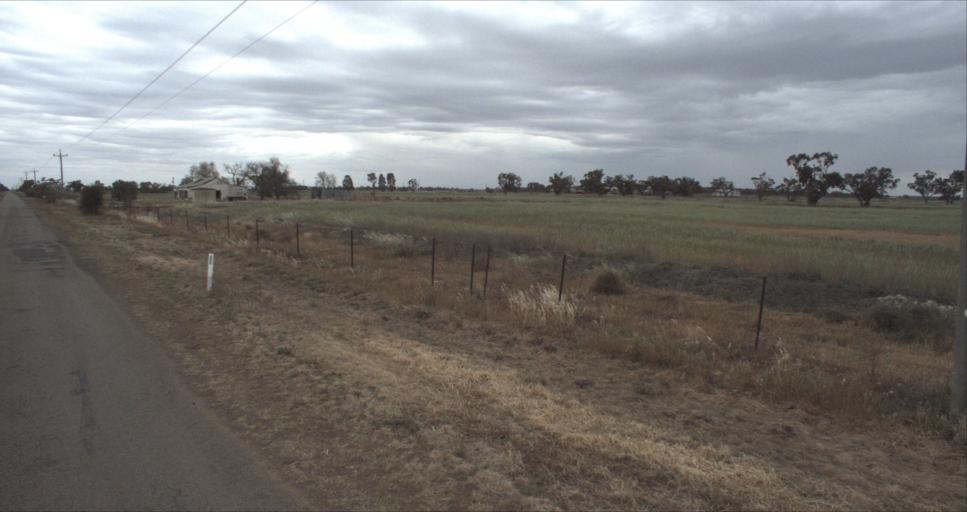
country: AU
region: New South Wales
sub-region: Leeton
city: Leeton
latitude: -34.4113
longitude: 146.3403
